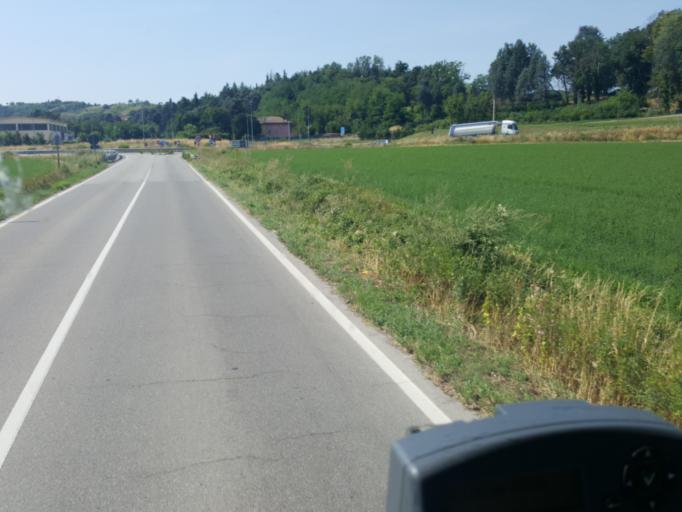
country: IT
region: Piedmont
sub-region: Provincia di Alessandria
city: Serravalle Scrivia
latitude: 44.7400
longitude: 8.8457
